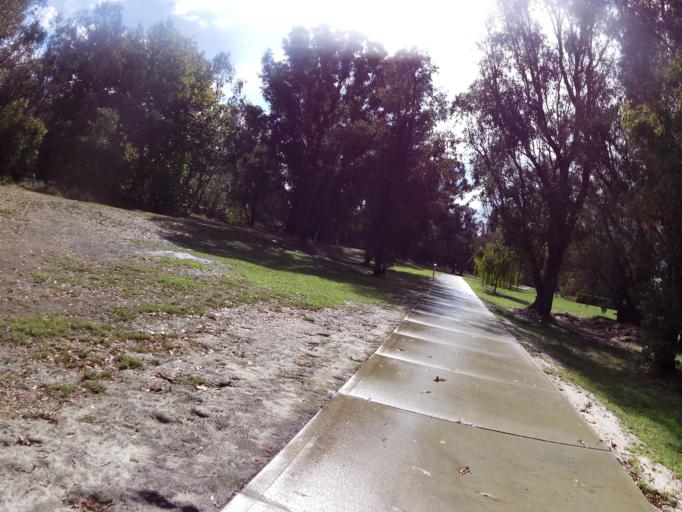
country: AU
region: Western Australia
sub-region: Donnybrook-Balingup
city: Donnybrook
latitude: -33.5737
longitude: 115.8258
